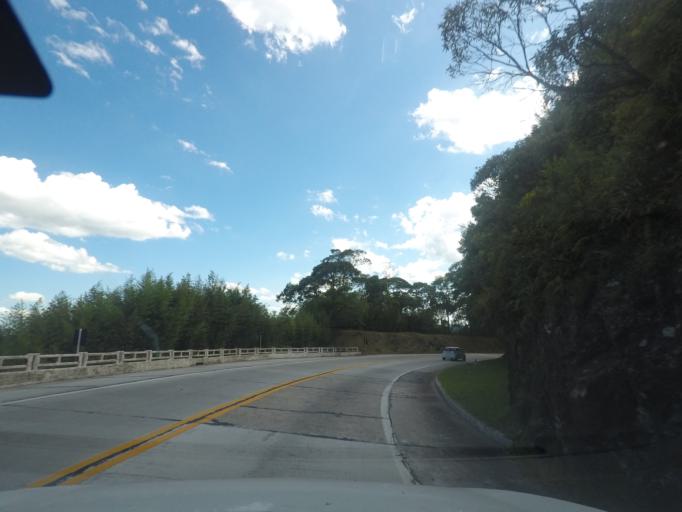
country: BR
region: Rio de Janeiro
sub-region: Guapimirim
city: Guapimirim
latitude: -22.4798
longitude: -42.9975
